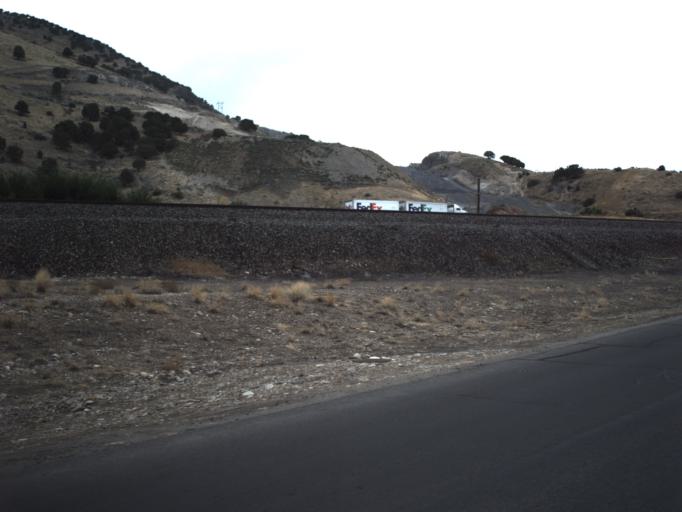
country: US
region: Utah
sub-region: Morgan County
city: Morgan
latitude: 41.0410
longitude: -111.6657
